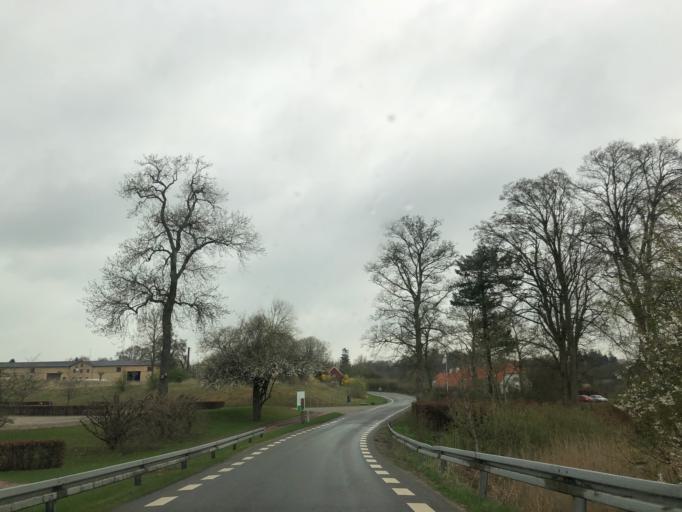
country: DK
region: Zealand
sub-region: Lejre Kommune
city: Kirke Hvalso
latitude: 55.5333
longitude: 11.8507
